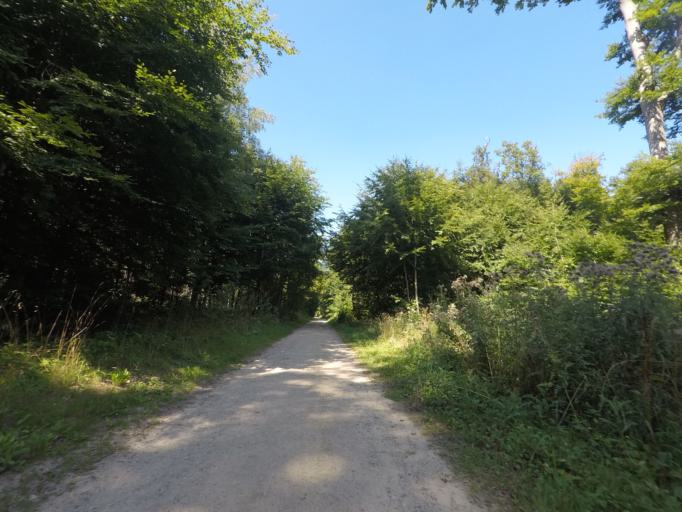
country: LU
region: Luxembourg
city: Bereldange
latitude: 49.6411
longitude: 6.1097
